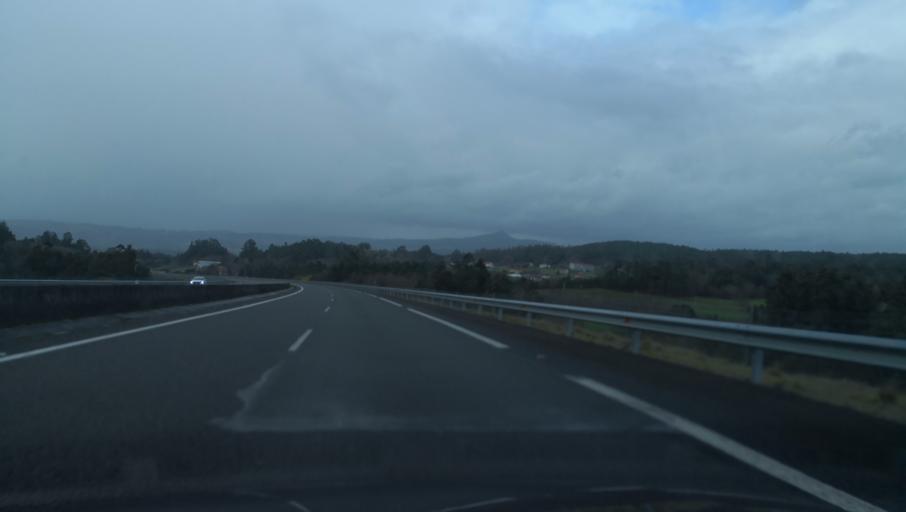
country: ES
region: Galicia
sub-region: Provincia da Coruna
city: Ribeira
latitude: 42.7441
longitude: -8.3750
